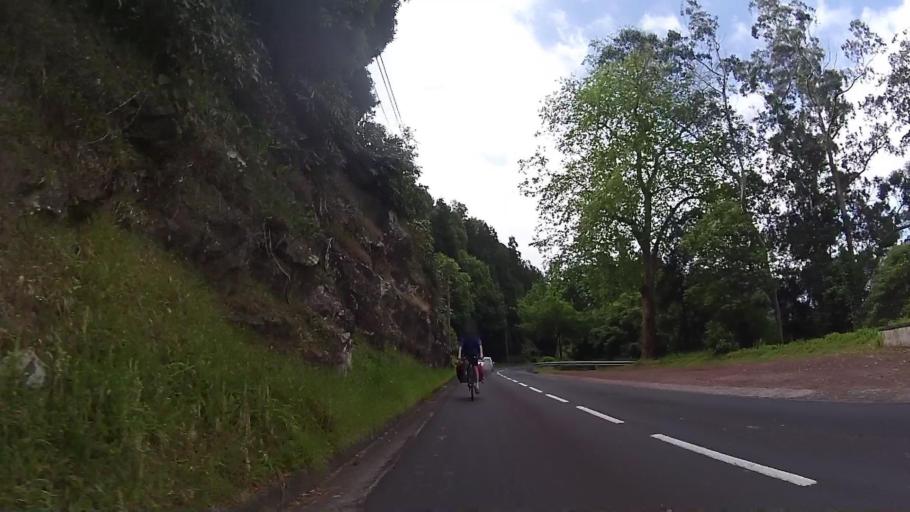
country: PT
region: Azores
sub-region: Povoacao
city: Furnas
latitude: 37.7655
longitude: -25.2887
